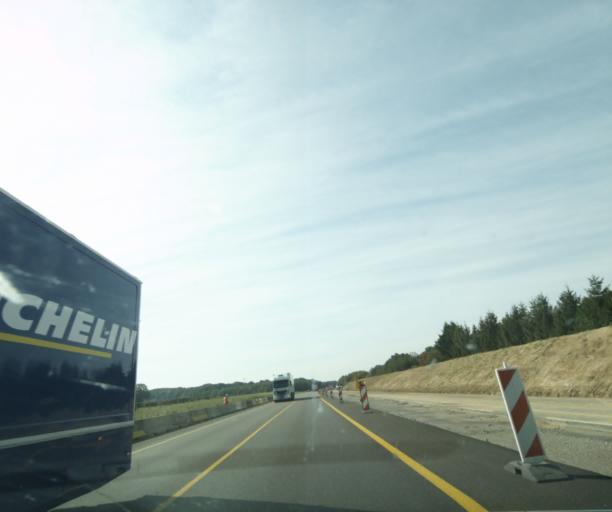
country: FR
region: Bourgogne
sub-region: Departement de Saone-et-Loire
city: Paray-le-Monial
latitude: 46.4979
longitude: 4.1587
